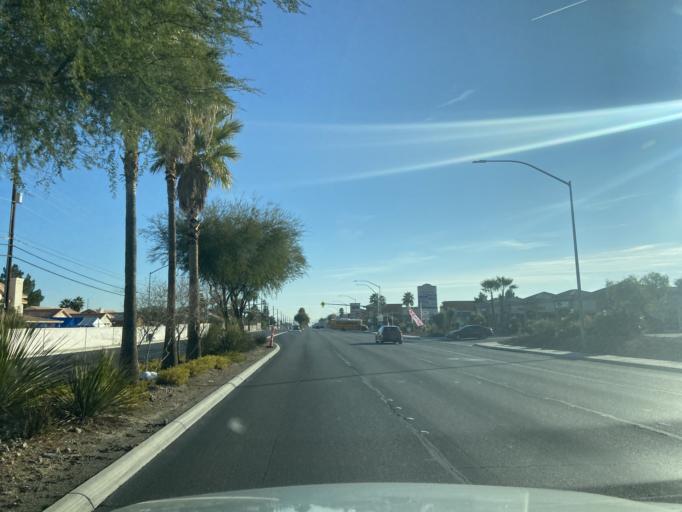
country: US
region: Nevada
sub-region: Clark County
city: North Las Vegas
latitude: 36.2394
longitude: -115.1865
